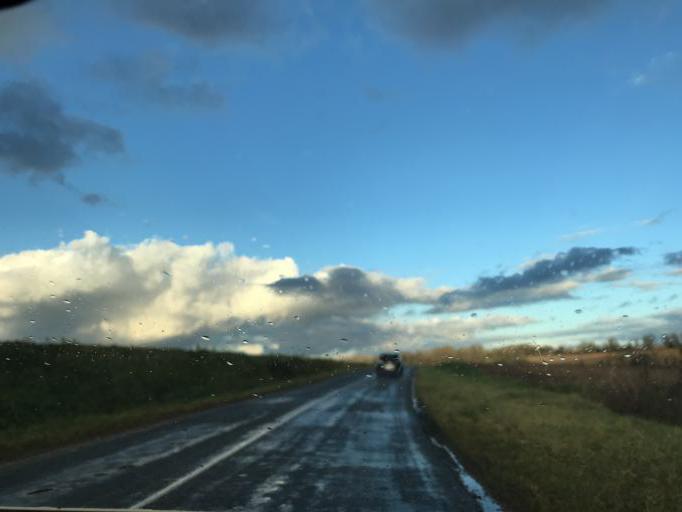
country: FR
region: Ile-de-France
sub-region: Departement de Seine-et-Marne
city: Juilly
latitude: 48.9926
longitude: 2.6970
